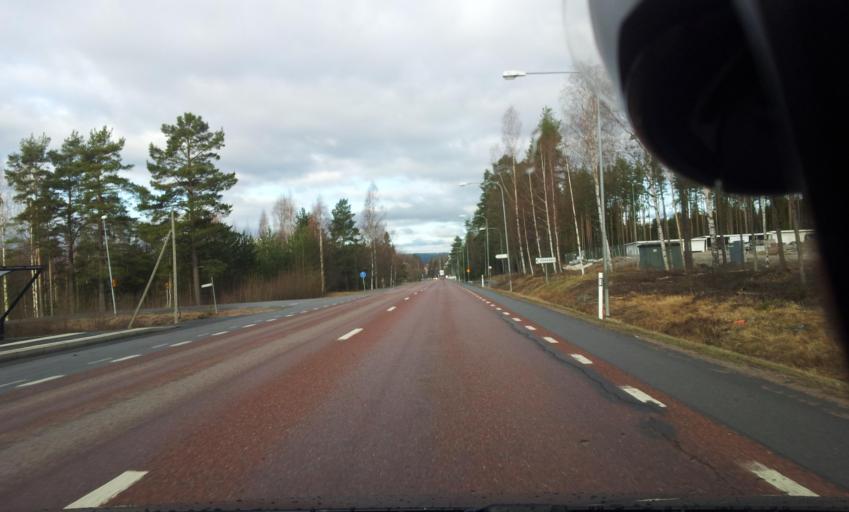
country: SE
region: Gaevleborg
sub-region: Ljusdals Kommun
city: Ljusdal
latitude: 61.8251
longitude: 16.1377
